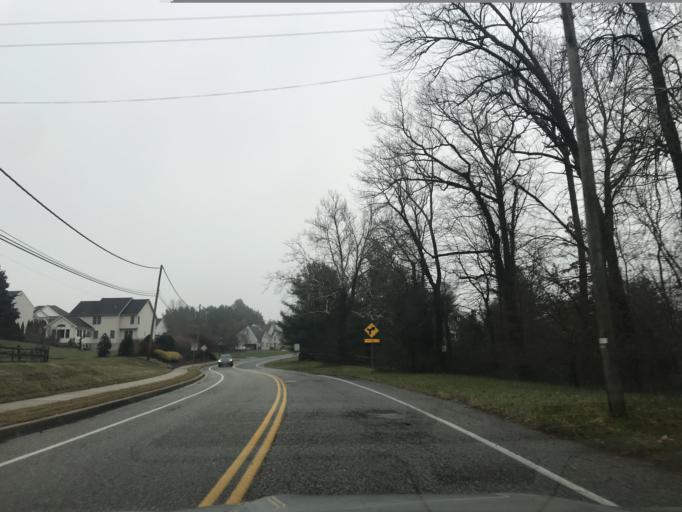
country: US
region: Maryland
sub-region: Harford County
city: South Bel Air
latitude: 39.5515
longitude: -76.3323
